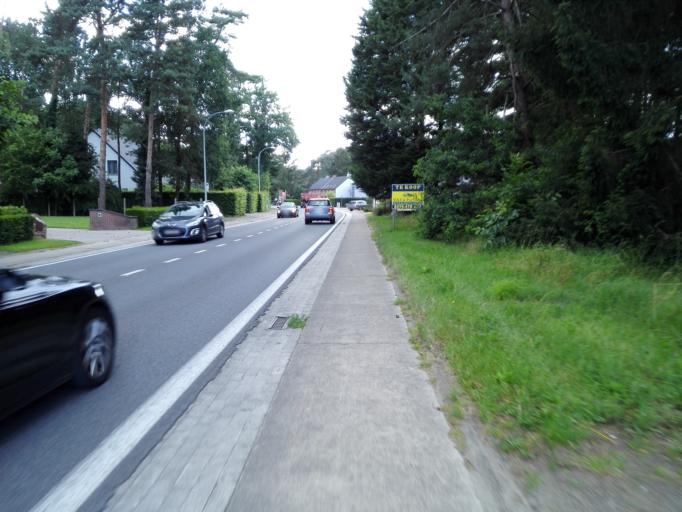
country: BE
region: Flanders
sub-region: Provincie Vlaams-Brabant
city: Keerbergen
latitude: 50.9965
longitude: 4.6686
